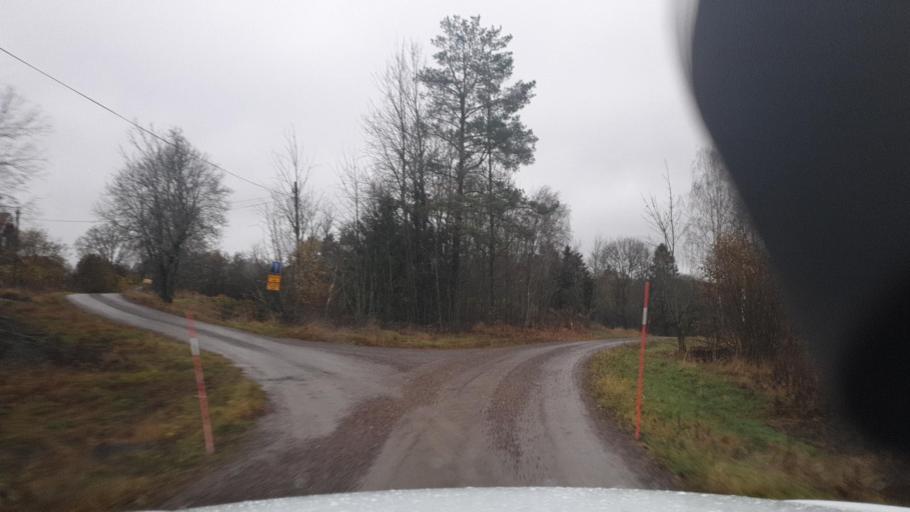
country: SE
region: Vaermland
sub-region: Eda Kommun
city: Charlottenberg
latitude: 59.7290
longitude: 12.1432
